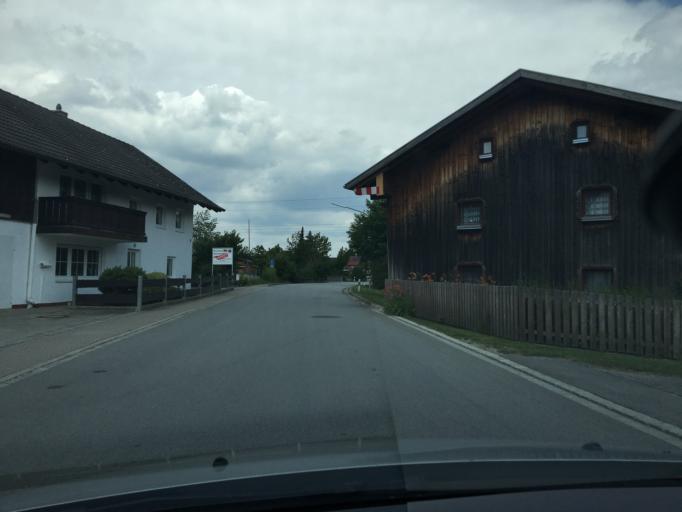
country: DE
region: Bavaria
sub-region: Lower Bavaria
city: Furth
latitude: 48.4282
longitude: 12.4169
